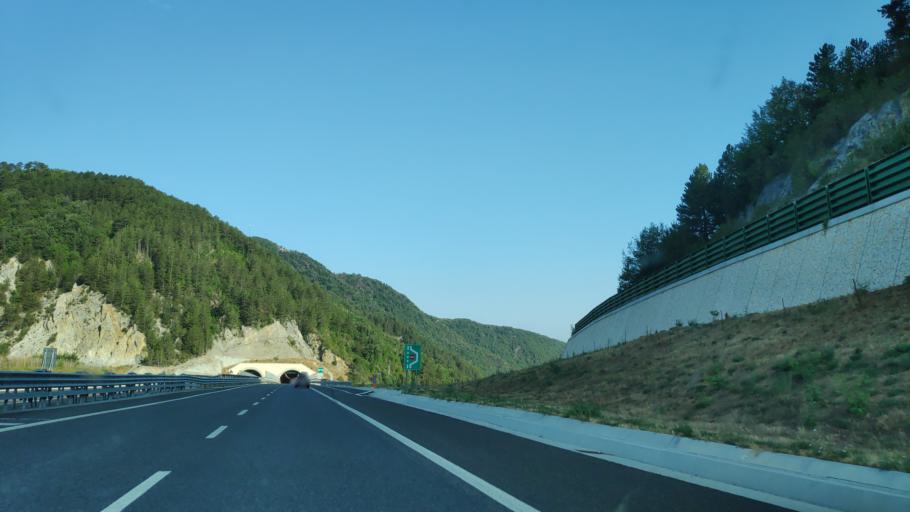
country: IT
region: Calabria
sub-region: Provincia di Cosenza
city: Mormanno
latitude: 39.8783
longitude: 15.9901
